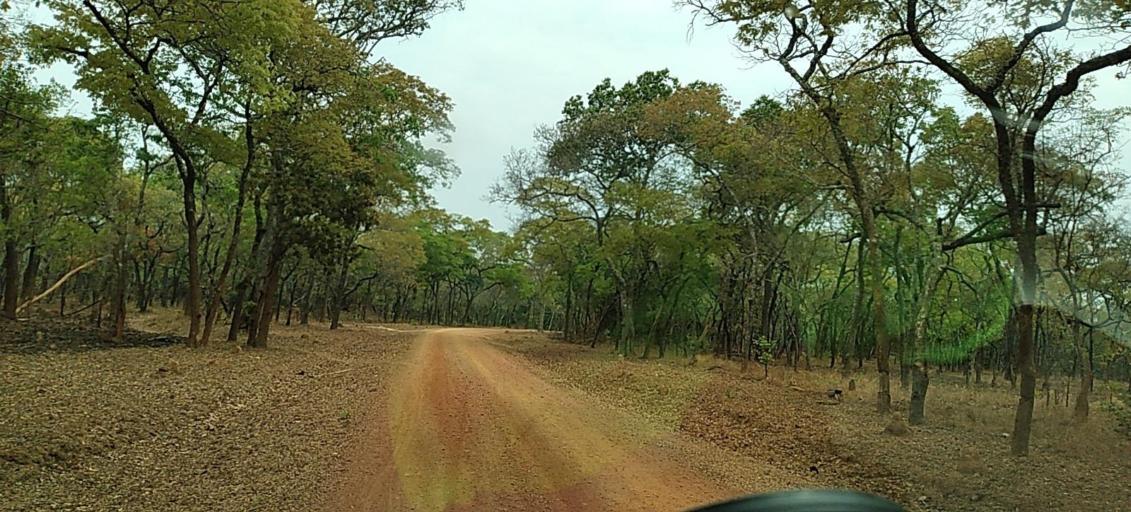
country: ZM
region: North-Western
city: Solwezi
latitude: -12.9227
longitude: 26.5612
